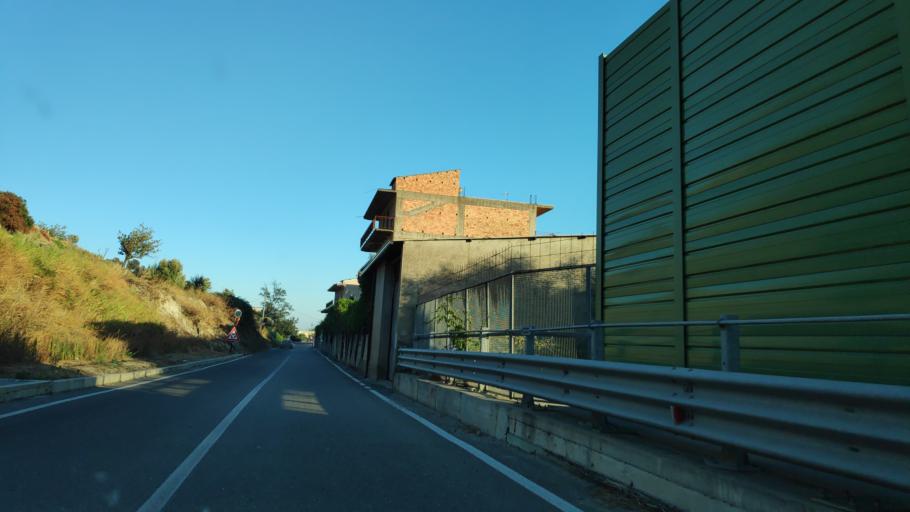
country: IT
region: Calabria
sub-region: Provincia di Reggio Calabria
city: Locri
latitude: 38.2378
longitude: 16.2367
